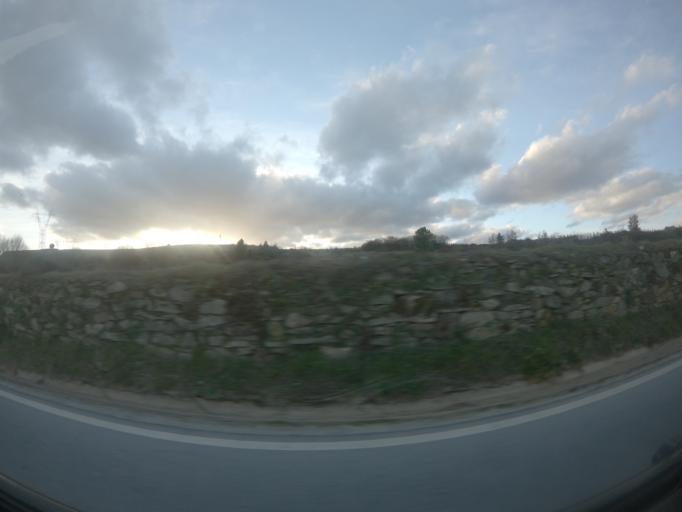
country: PT
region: Braganca
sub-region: Carrazeda de Ansiaes
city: Carrazeda de Anciaes
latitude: 41.2264
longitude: -7.3081
